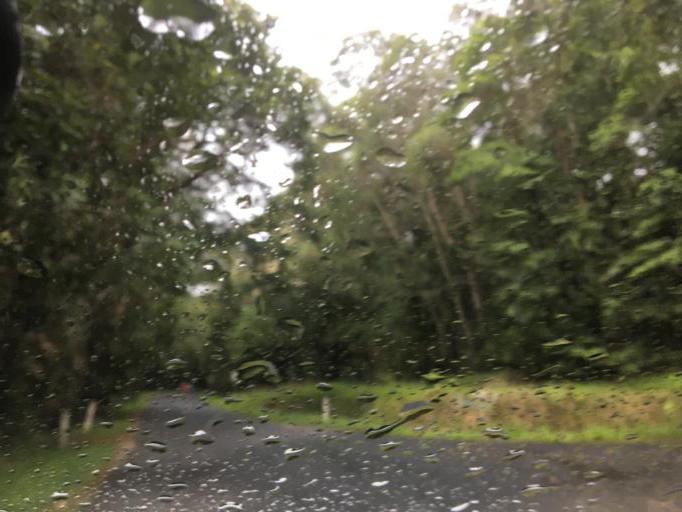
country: AU
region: Queensland
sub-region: Tablelands
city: Kuranda
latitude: -16.8330
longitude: 145.6341
